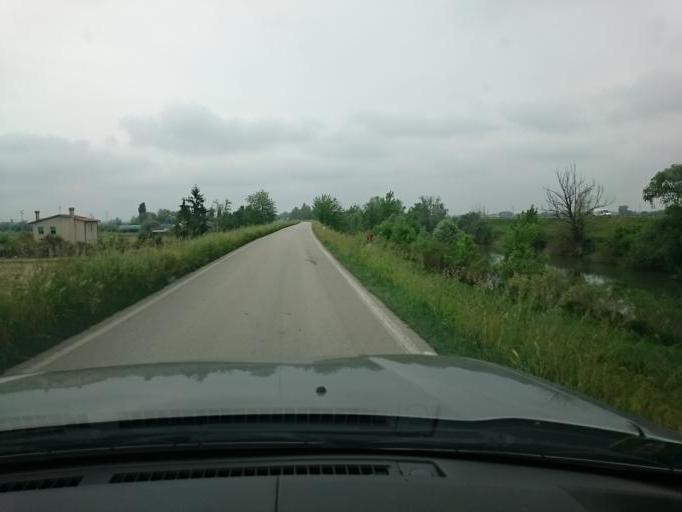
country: IT
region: Veneto
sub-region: Provincia di Padova
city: Campagnola
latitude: 45.2573
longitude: 11.9898
